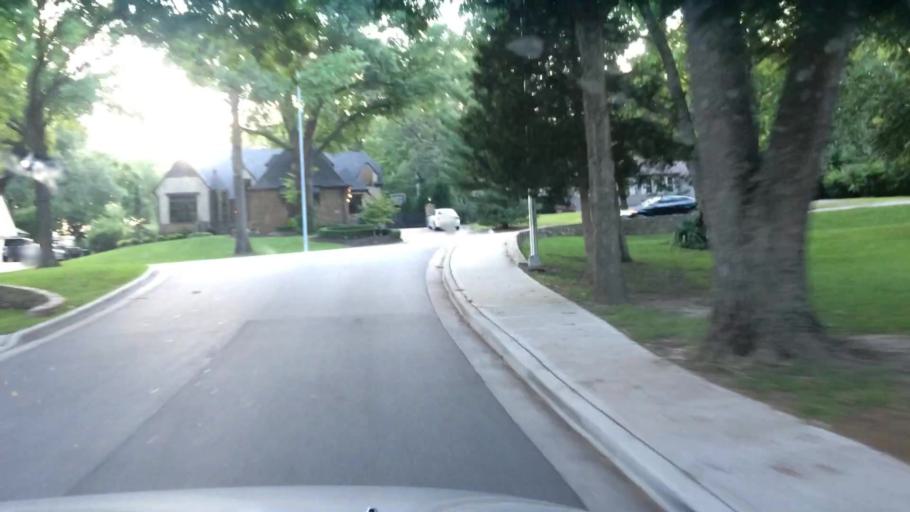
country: US
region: Kansas
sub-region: Johnson County
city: Leawood
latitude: 38.9742
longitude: -94.6117
